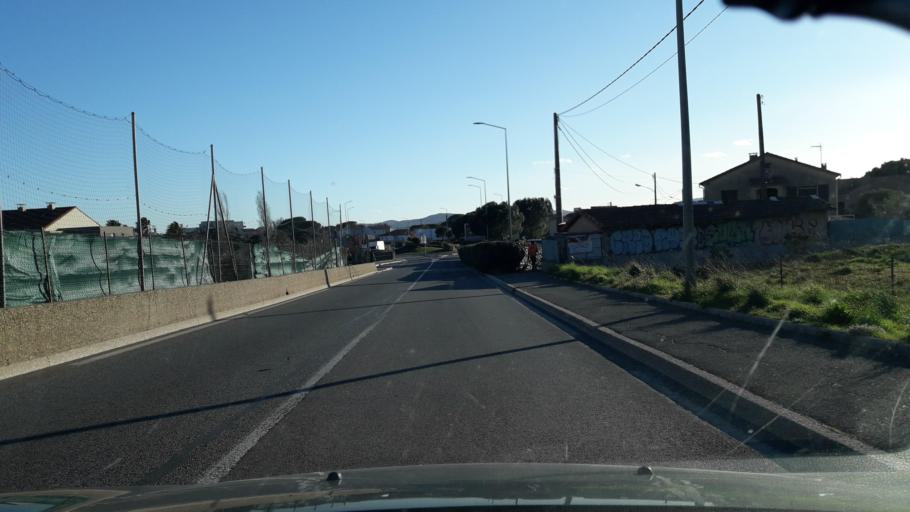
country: FR
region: Provence-Alpes-Cote d'Azur
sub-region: Departement du Var
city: Frejus
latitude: 43.4549
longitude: 6.7273
